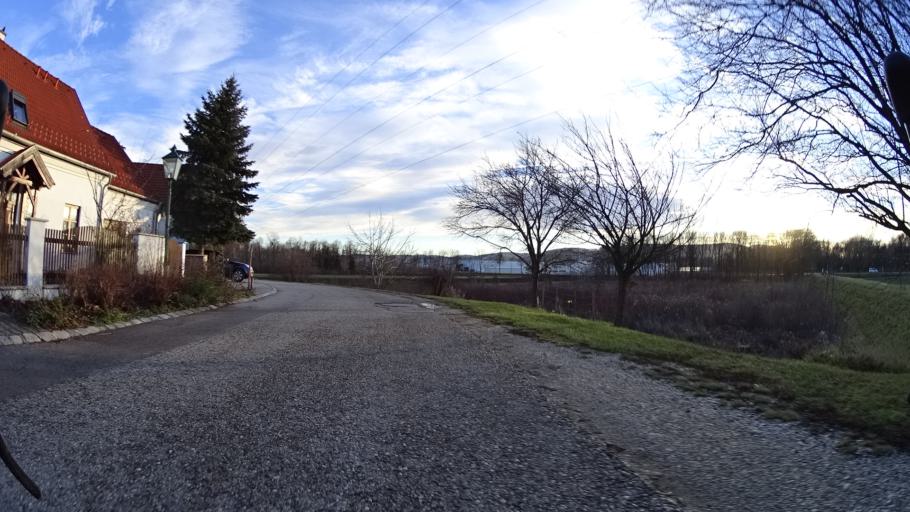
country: AT
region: Lower Austria
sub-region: Politischer Bezirk Korneuburg
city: Leobendorf
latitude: 48.3728
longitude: 16.2980
